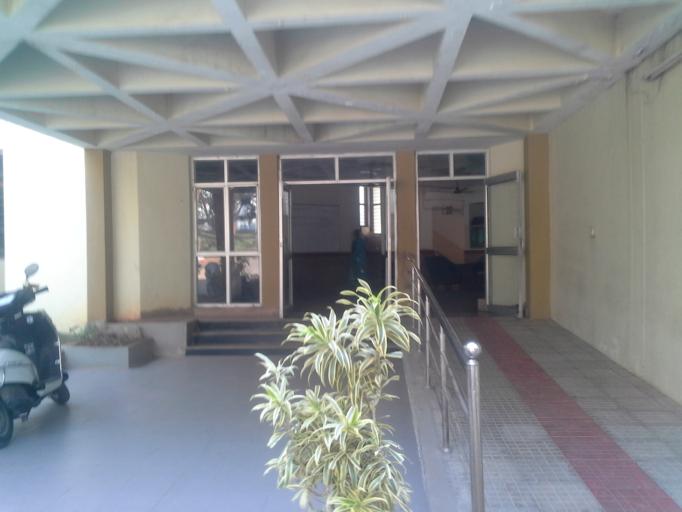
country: IN
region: Telangana
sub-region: Hyderabad
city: Hyderabad
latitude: 17.3116
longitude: 78.4042
